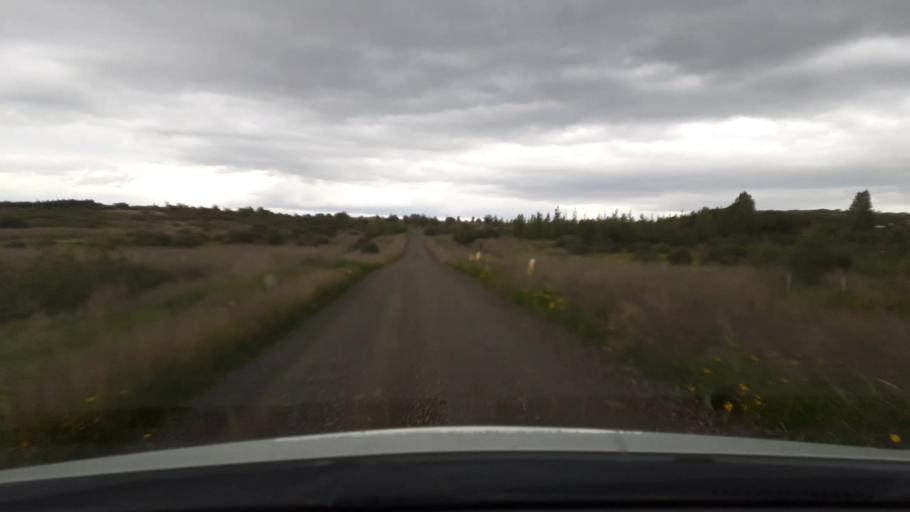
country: IS
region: West
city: Borgarnes
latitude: 64.6412
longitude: -21.7548
